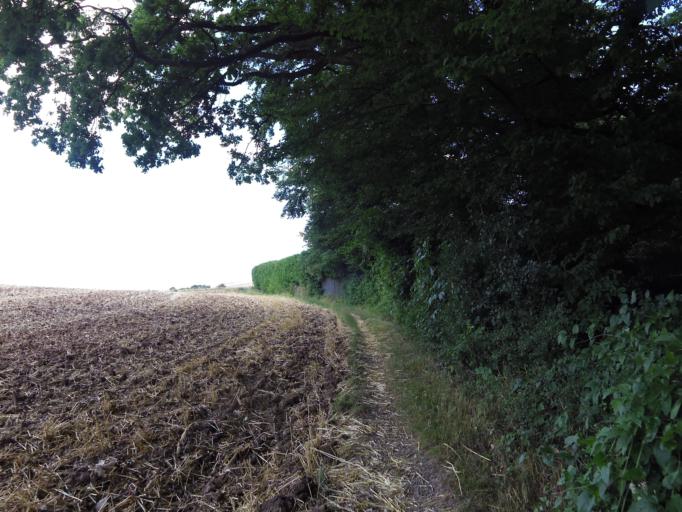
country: DE
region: Bavaria
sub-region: Regierungsbezirk Unterfranken
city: Hochberg
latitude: 49.7780
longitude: 9.8967
